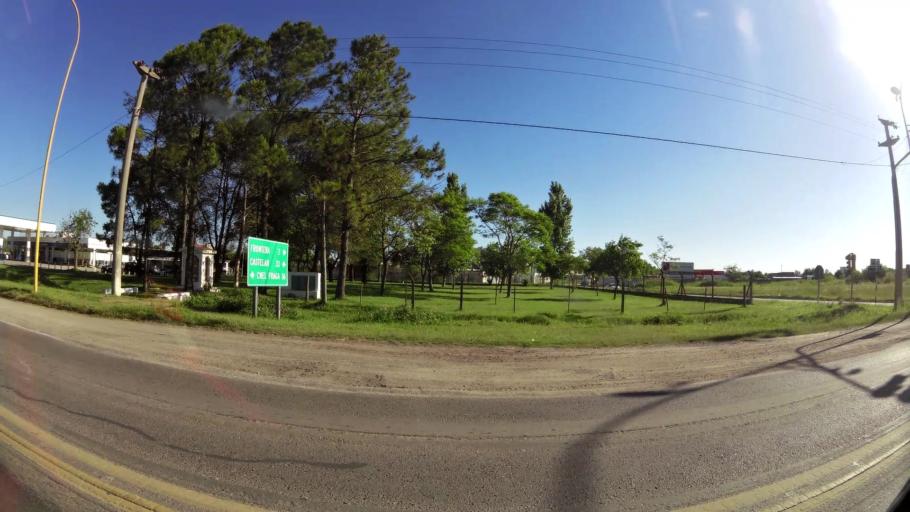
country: AR
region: Cordoba
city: San Francisco
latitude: -31.4198
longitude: -62.0647
